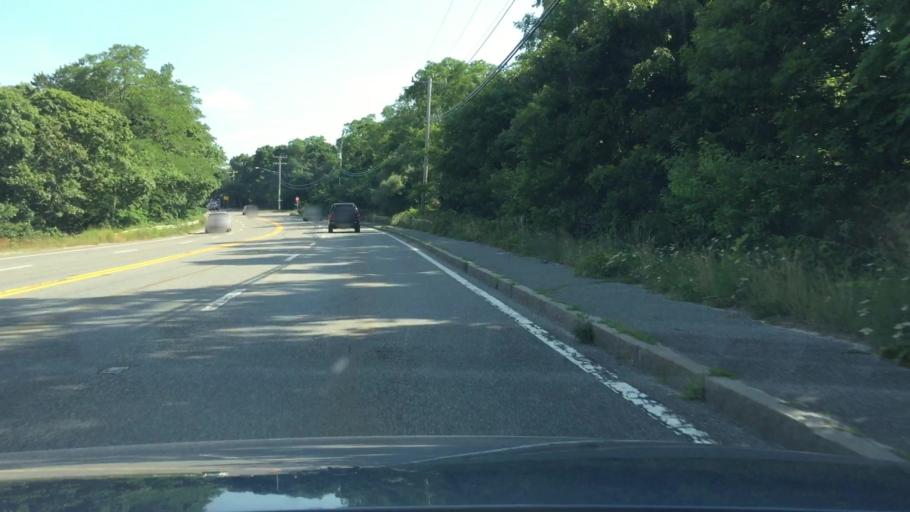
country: US
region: Massachusetts
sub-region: Barnstable County
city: North Eastham
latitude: 41.8500
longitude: -69.9877
